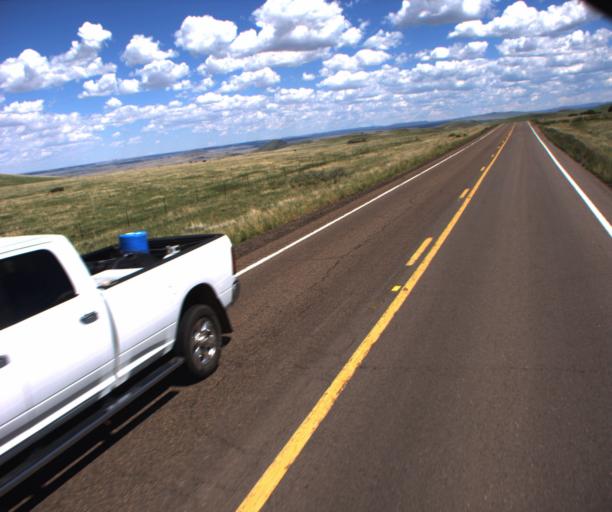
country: US
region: Arizona
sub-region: Apache County
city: Springerville
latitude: 34.2187
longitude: -109.4740
